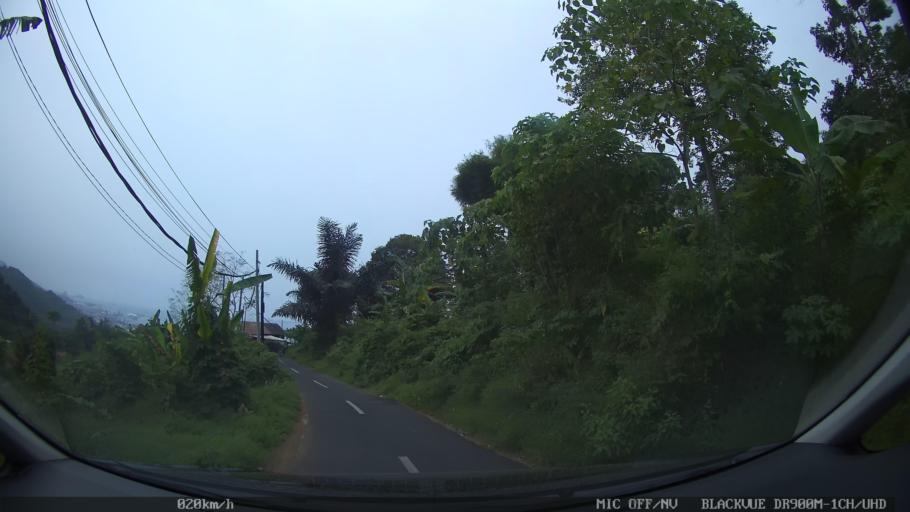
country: ID
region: Lampung
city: Panjang
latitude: -5.4367
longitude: 105.3121
